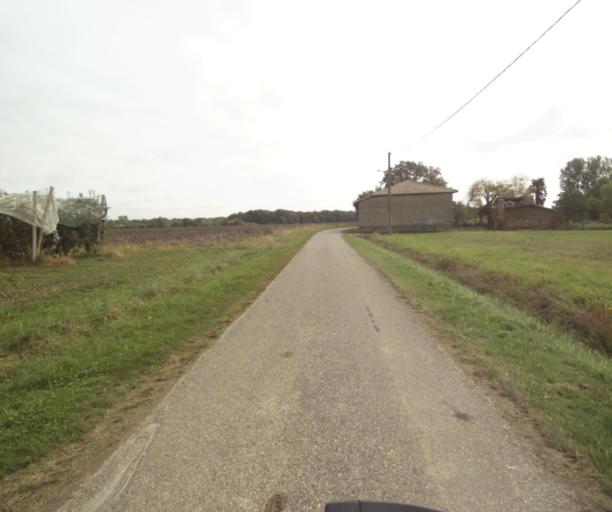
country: FR
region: Midi-Pyrenees
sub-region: Departement du Tarn-et-Garonne
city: Finhan
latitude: 43.9154
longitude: 1.2437
